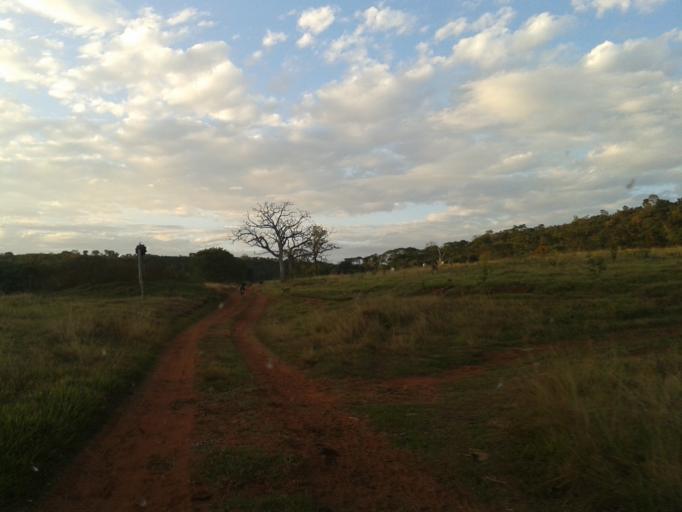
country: BR
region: Minas Gerais
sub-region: Campina Verde
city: Campina Verde
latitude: -19.3515
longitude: -49.6676
